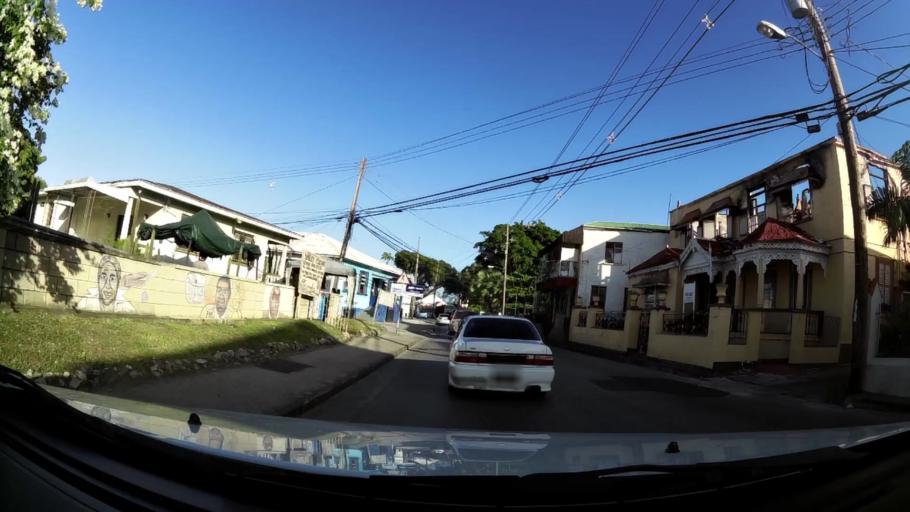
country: BB
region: Saint Michael
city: Bridgetown
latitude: 13.0841
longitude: -59.6081
